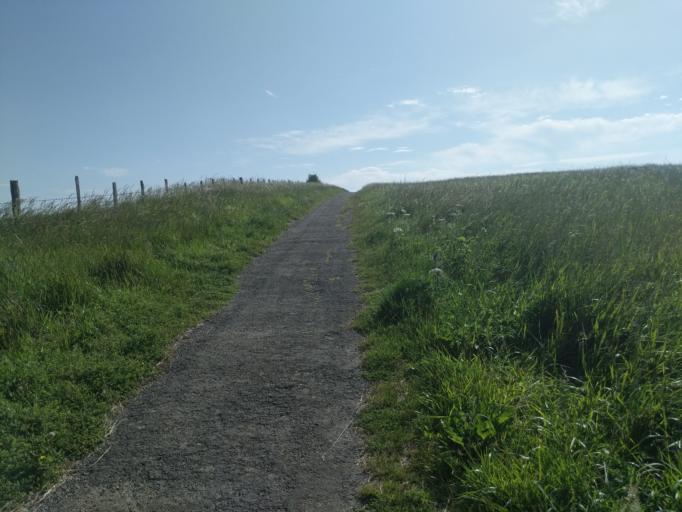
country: GB
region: England
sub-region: Kent
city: Dover
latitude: 51.1022
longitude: 1.2461
